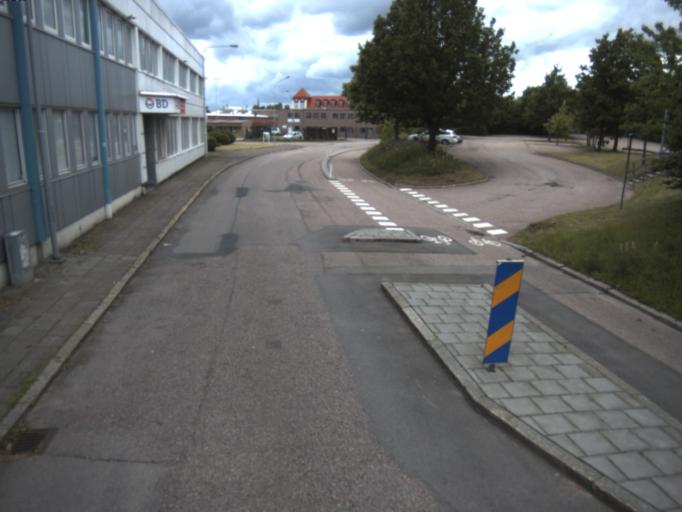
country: SE
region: Skane
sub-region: Helsingborg
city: Helsingborg
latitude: 56.0304
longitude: 12.7175
